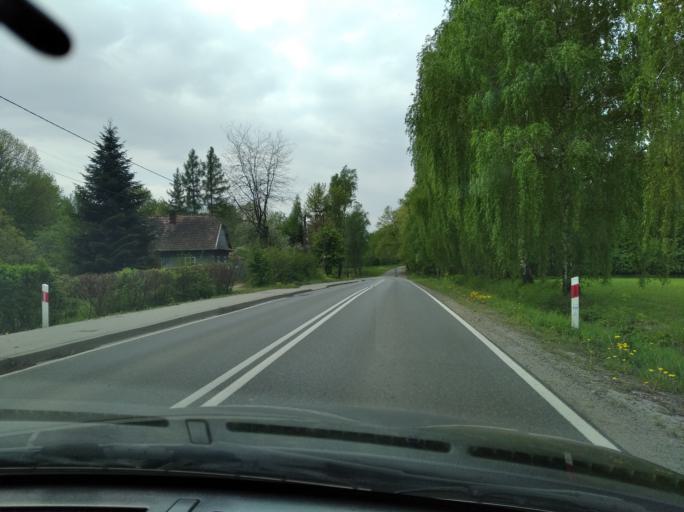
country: PL
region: Lesser Poland Voivodeship
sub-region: Powiat tarnowski
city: Tarnowiec
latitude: 49.9628
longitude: 20.9917
